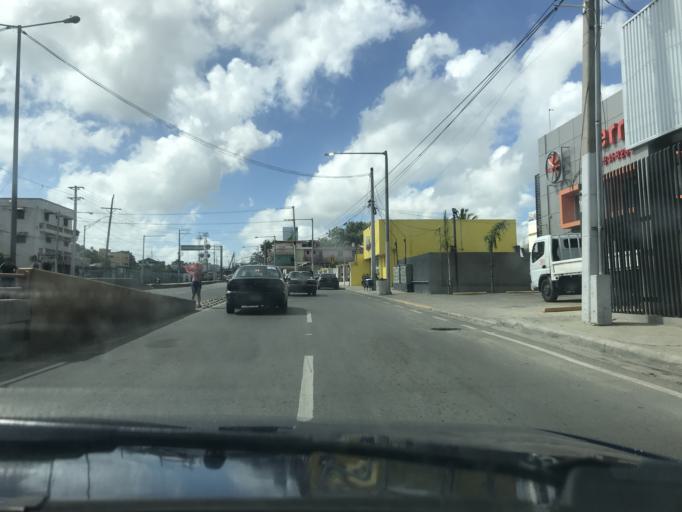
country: DO
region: Santiago
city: Santiago de los Caballeros
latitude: 19.4849
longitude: -70.7310
